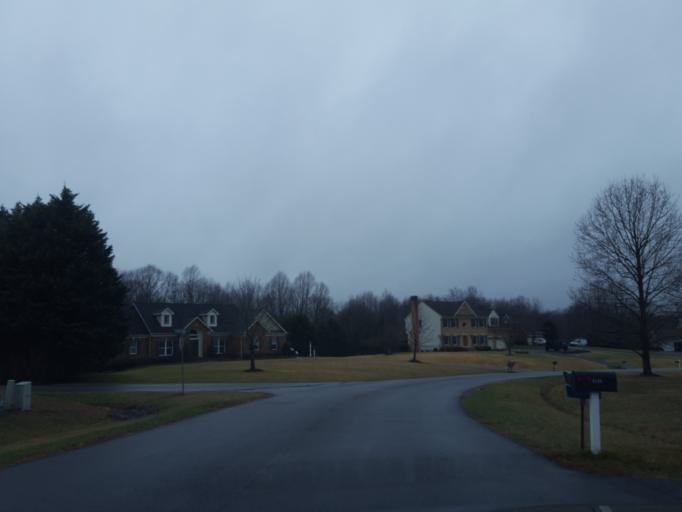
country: US
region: Maryland
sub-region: Calvert County
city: Chesapeake Beach
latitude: 38.6153
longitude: -76.5406
